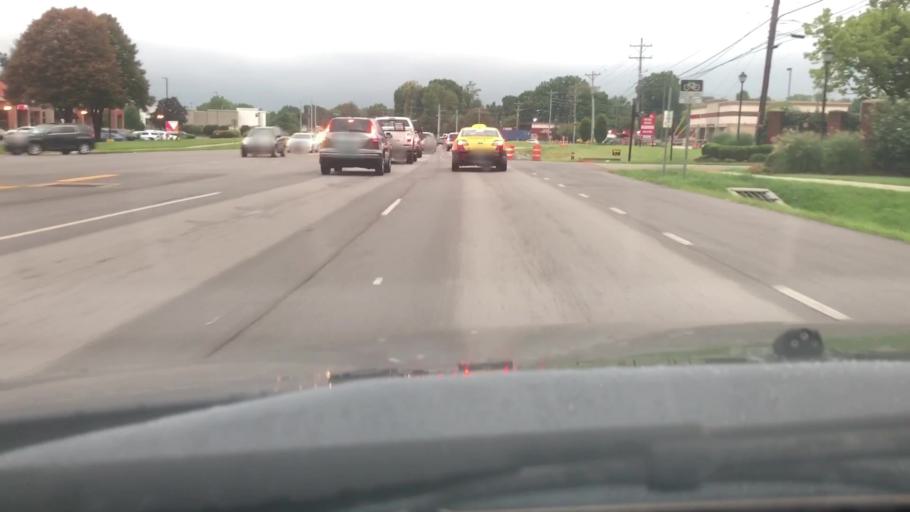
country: US
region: Kentucky
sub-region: Jefferson County
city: Hurstbourne Acres
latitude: 38.2142
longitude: -85.5889
